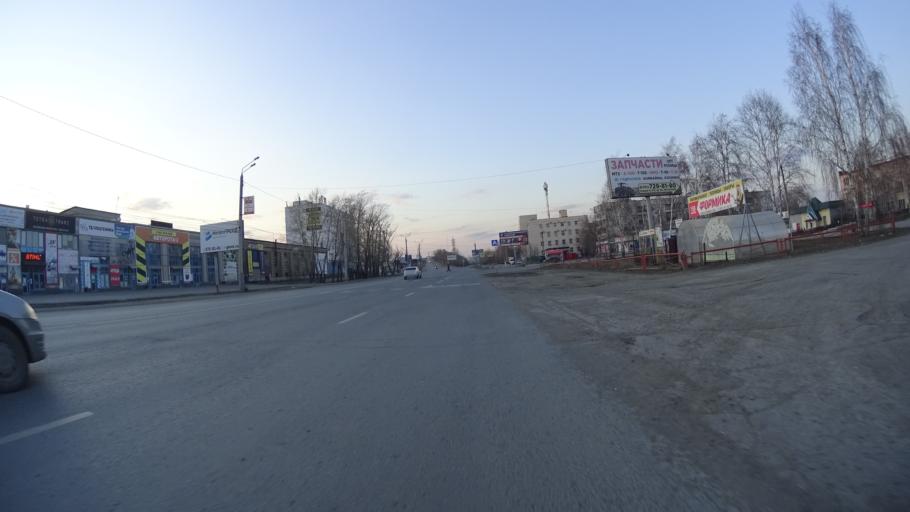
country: RU
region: Chelyabinsk
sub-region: Gorod Chelyabinsk
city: Chelyabinsk
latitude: 55.1115
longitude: 61.3869
